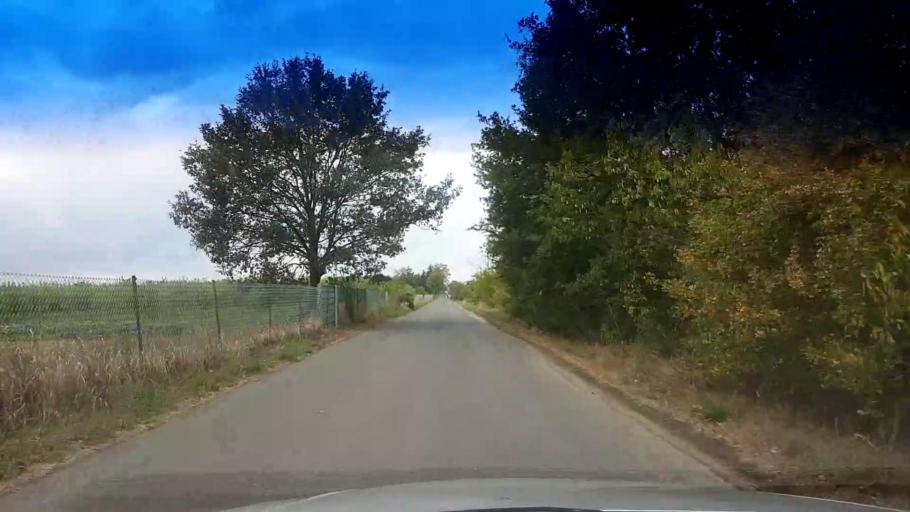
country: DE
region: Bavaria
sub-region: Upper Franconia
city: Bamberg
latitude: 49.8746
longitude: 10.9267
